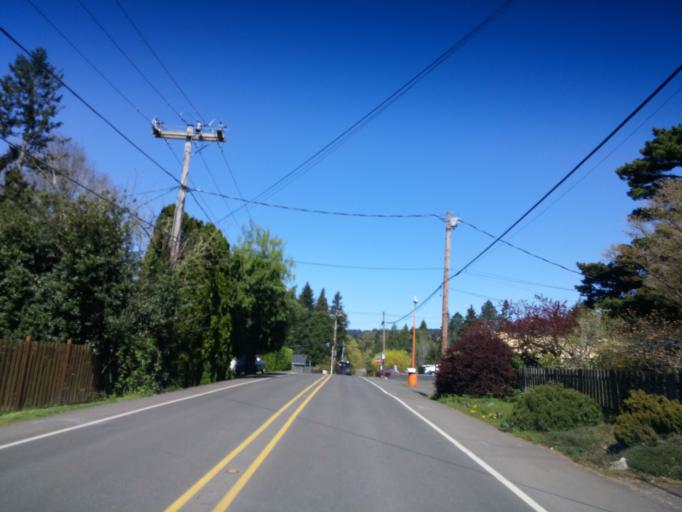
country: US
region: Oregon
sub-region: Washington County
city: West Haven
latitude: 45.5250
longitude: -122.7871
